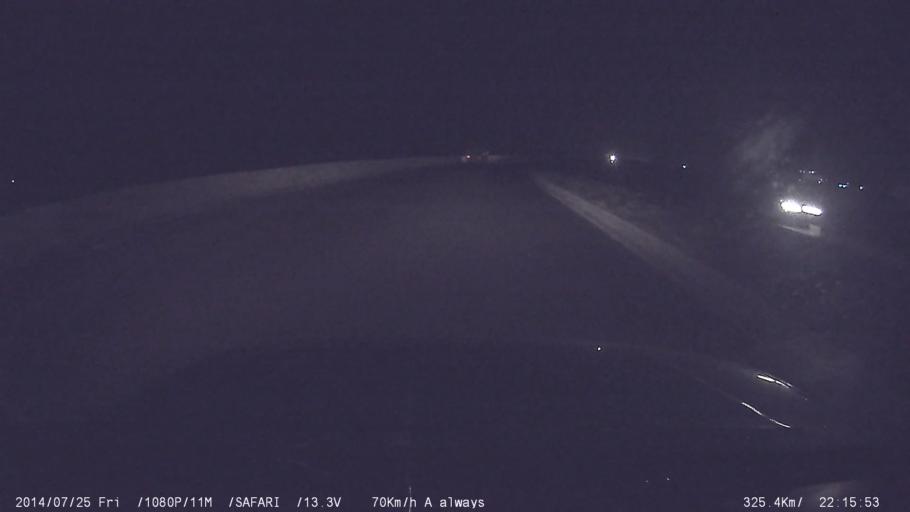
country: IN
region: Tamil Nadu
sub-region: Tiruppur
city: Avinashi
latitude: 11.1284
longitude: 77.1980
